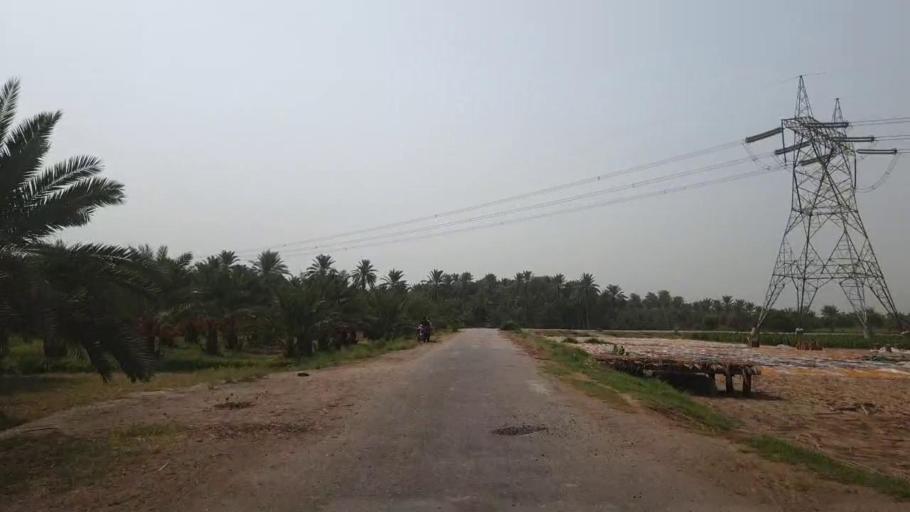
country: PK
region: Sindh
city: Gambat
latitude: 27.4138
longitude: 68.5536
